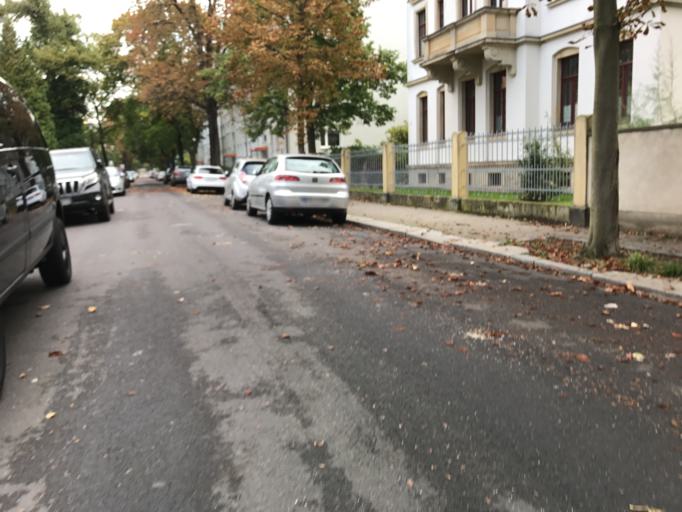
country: DE
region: Saxony
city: Albertstadt
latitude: 51.0483
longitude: 13.7851
